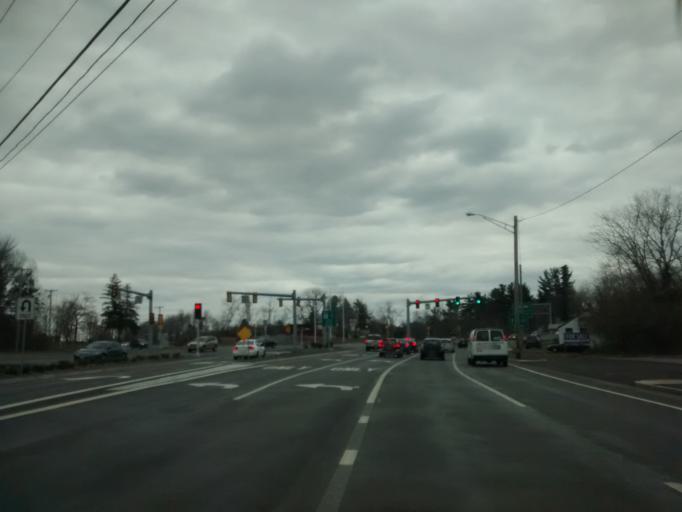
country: US
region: Massachusetts
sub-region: Worcester County
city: Auburn
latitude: 42.1795
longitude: -71.8701
